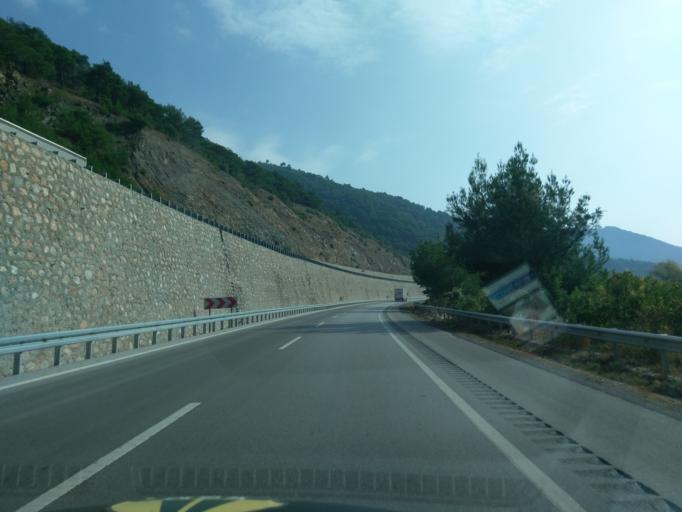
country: TR
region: Amasya
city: Akdag
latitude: 40.7532
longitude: 36.0641
